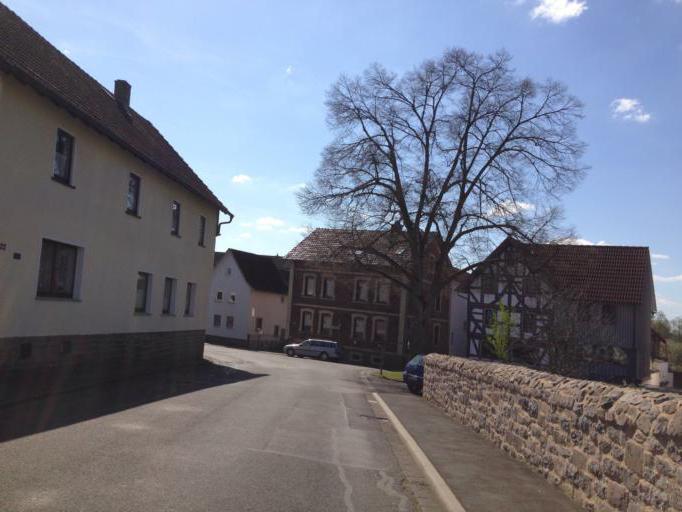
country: DE
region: Hesse
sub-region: Regierungsbezirk Giessen
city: Grunberg
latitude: 50.5523
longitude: 8.9202
